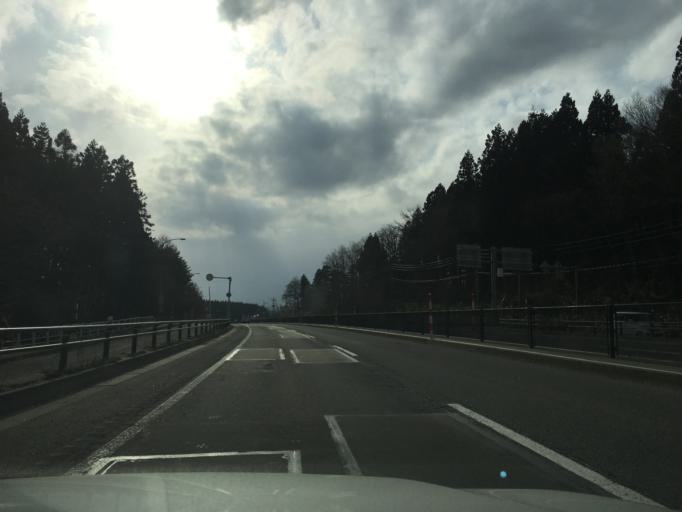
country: JP
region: Aomori
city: Aomori Shi
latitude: 40.8348
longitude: 140.6744
